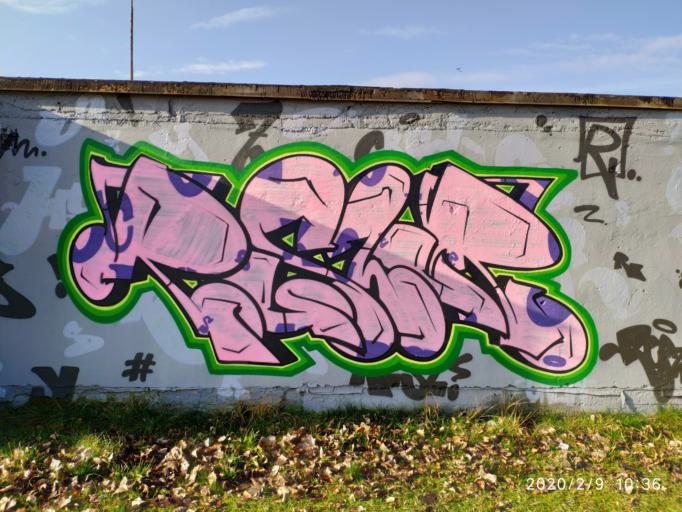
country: PL
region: Lubusz
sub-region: Powiat nowosolski
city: Nowa Sol
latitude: 51.8048
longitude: 15.6970
